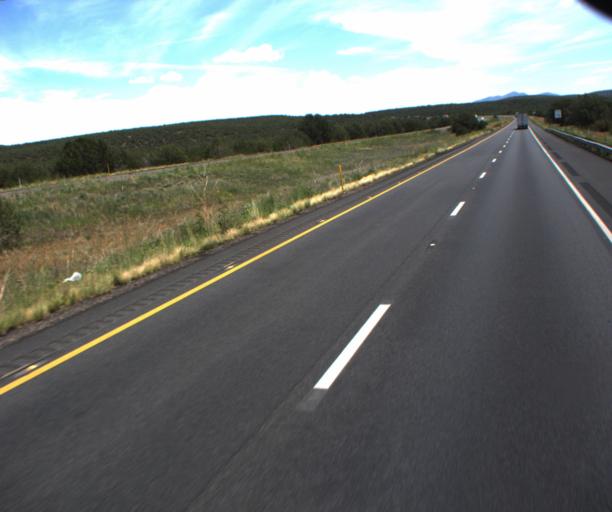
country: US
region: Arizona
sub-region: Coconino County
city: Williams
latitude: 35.2136
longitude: -112.4173
